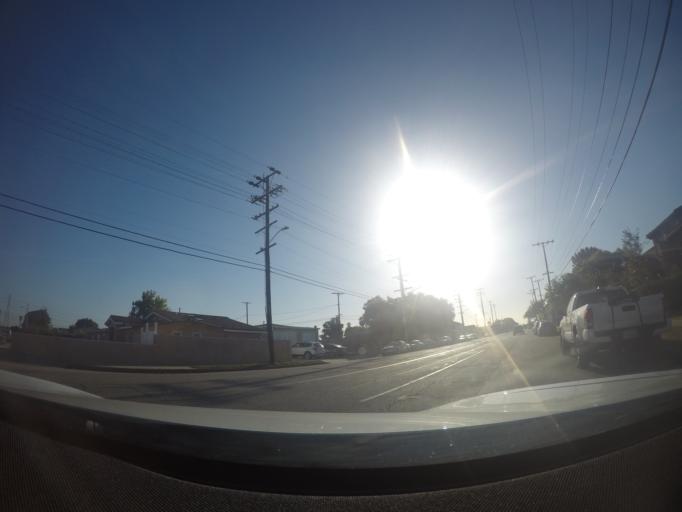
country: US
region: California
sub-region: Los Angeles County
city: Lawndale
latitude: 33.8655
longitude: -118.3492
